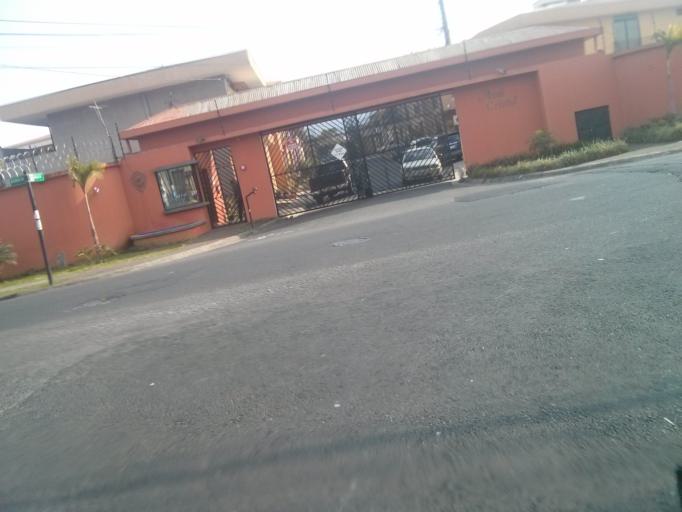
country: CR
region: San Jose
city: San Pedro
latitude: 9.9070
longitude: -84.0646
